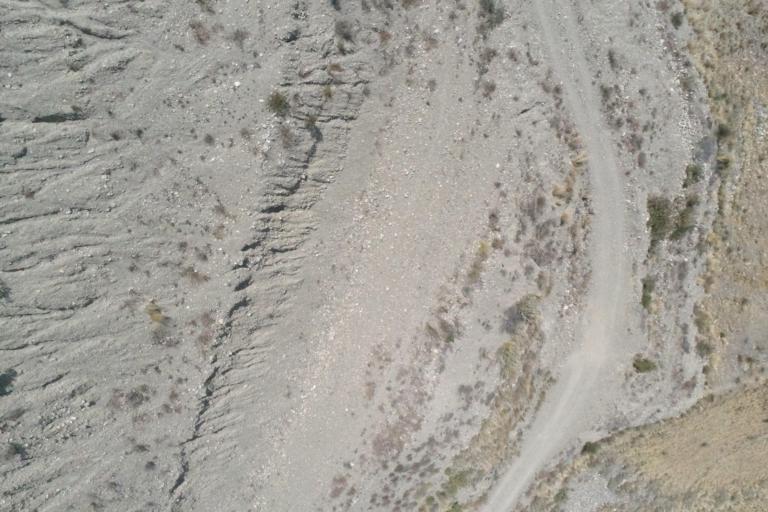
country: BO
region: La Paz
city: La Paz
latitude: -16.4712
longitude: -68.0985
